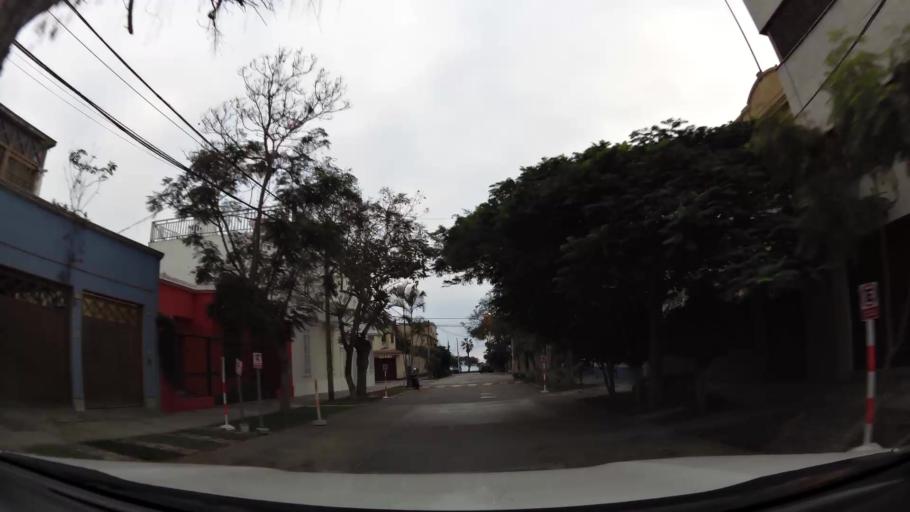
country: PE
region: Lima
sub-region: Lima
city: Surco
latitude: -12.1424
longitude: -77.0240
